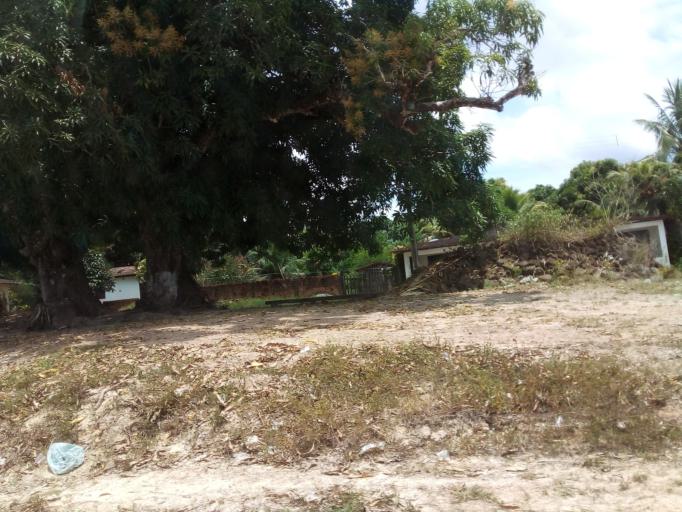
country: BR
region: Maranhao
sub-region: Anajatuba
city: Anajatuba
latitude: -3.0352
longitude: -44.3471
